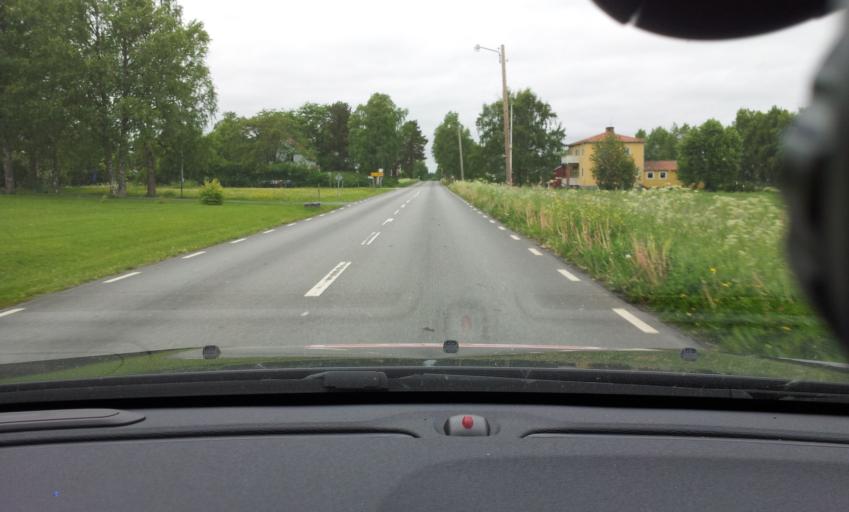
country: SE
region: Jaemtland
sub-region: Bergs Kommun
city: Hoverberg
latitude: 63.0676
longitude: 14.3234
